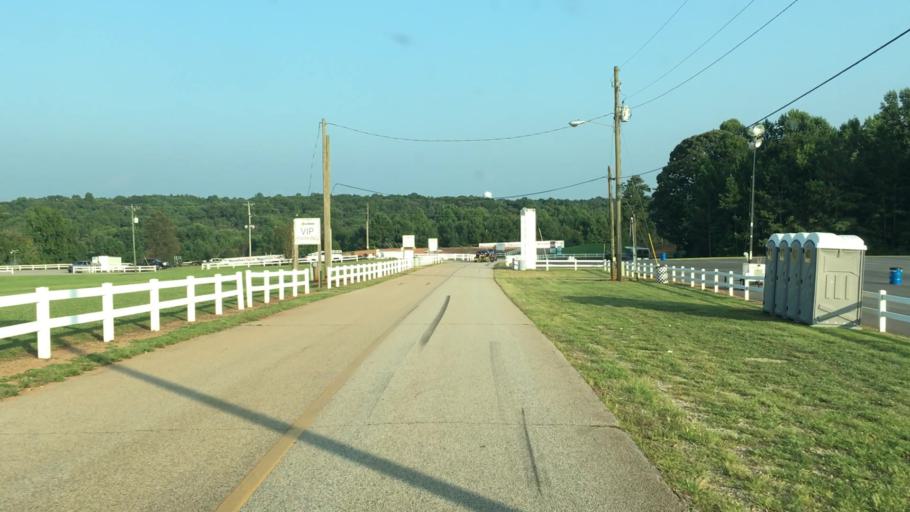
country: US
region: Georgia
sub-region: Jackson County
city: Braselton
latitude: 34.1475
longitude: -83.8144
